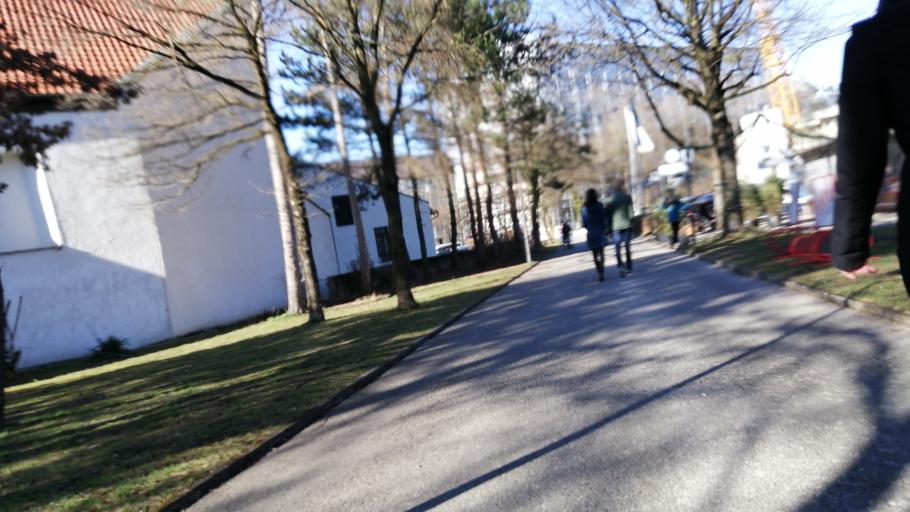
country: DE
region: Bavaria
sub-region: Upper Bavaria
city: Neuried
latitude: 48.1276
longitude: 11.5151
